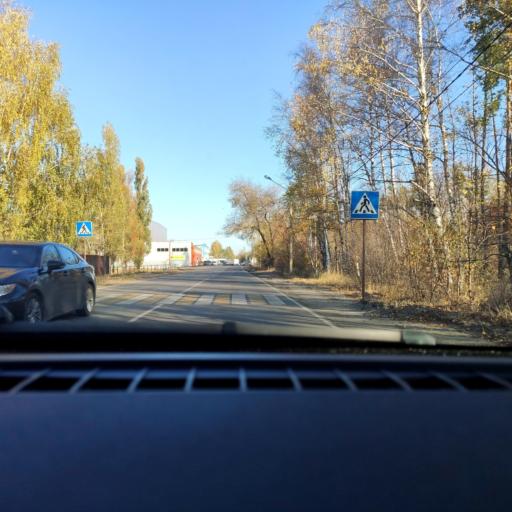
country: RU
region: Voronezj
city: Somovo
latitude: 51.7176
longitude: 39.2942
